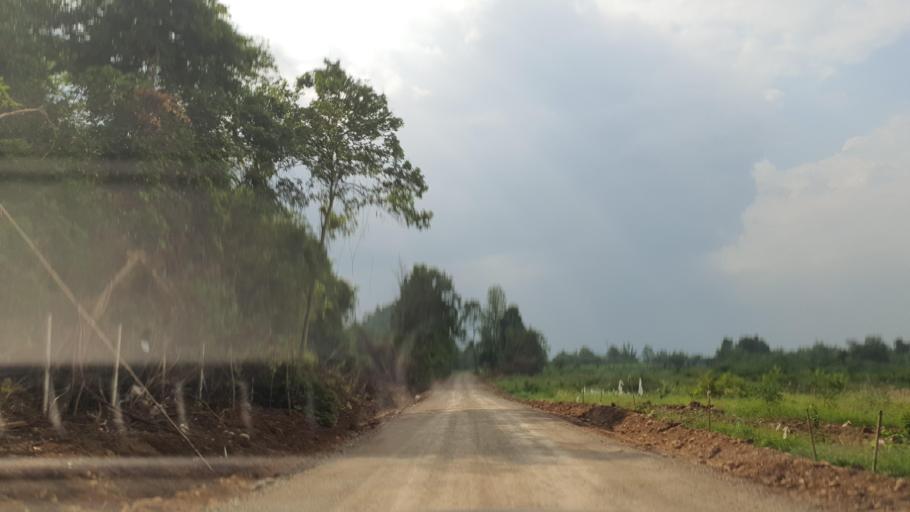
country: TH
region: Sukhothai
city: Thung Saliam
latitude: 17.2568
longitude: 99.5408
